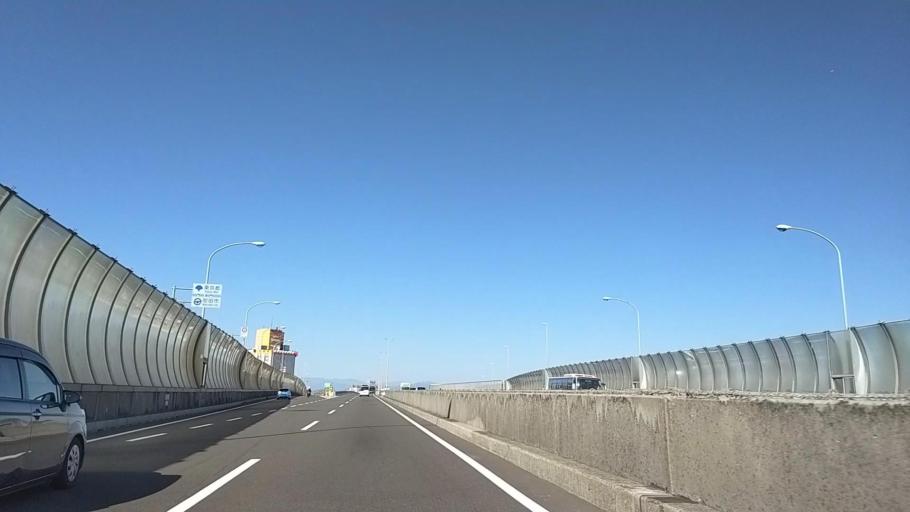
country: JP
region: Kanagawa
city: Minami-rinkan
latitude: 35.5042
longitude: 139.4852
